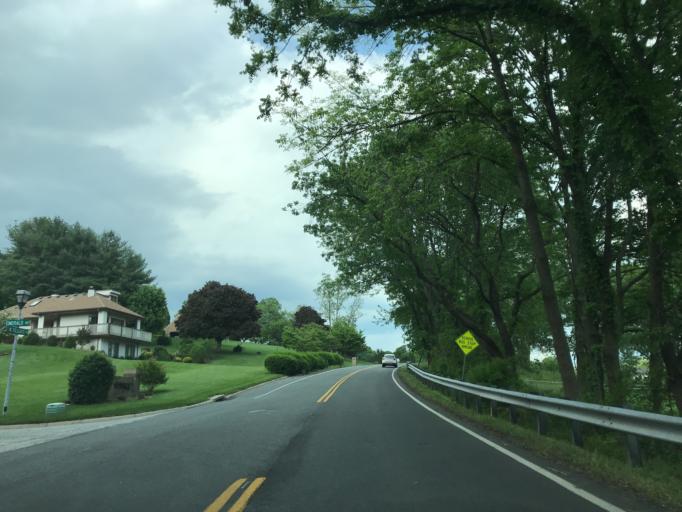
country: US
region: Maryland
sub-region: Harford County
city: Bel Air North
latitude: 39.5297
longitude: -76.3822
